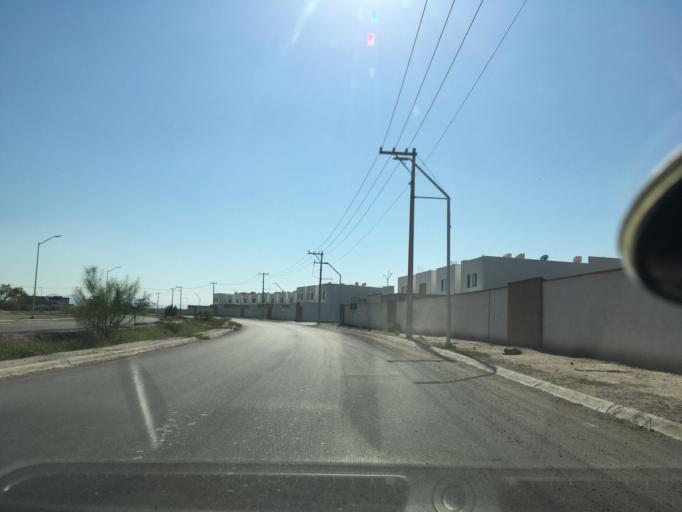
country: MX
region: Coahuila
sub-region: Torreon
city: Fraccionamiento la Noria
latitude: 25.5711
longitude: -103.3624
